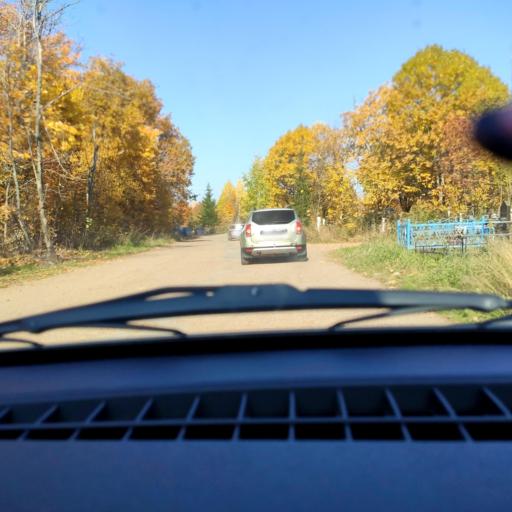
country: RU
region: Bashkortostan
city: Mikhaylovka
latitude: 54.8128
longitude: 55.8667
